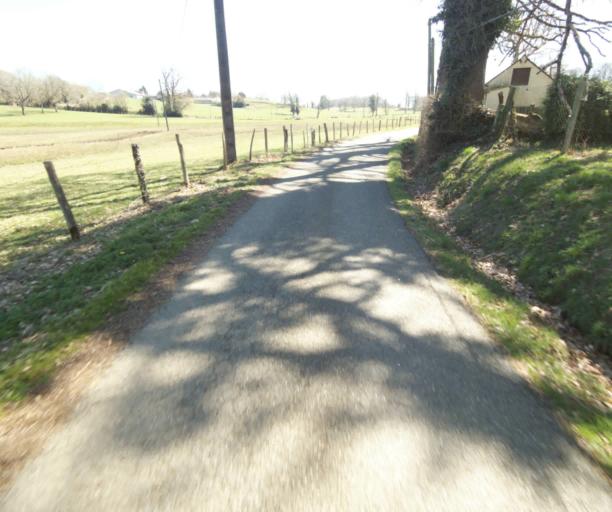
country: FR
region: Limousin
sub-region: Departement de la Correze
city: Uzerche
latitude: 45.4005
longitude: 1.6305
